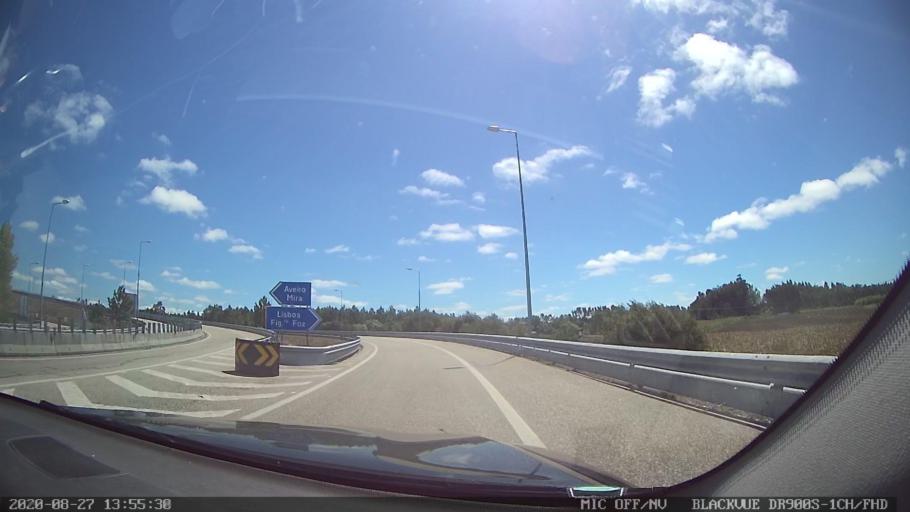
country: PT
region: Coimbra
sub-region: Montemor-O-Velho
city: Arazede
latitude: 40.3270
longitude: -8.7251
